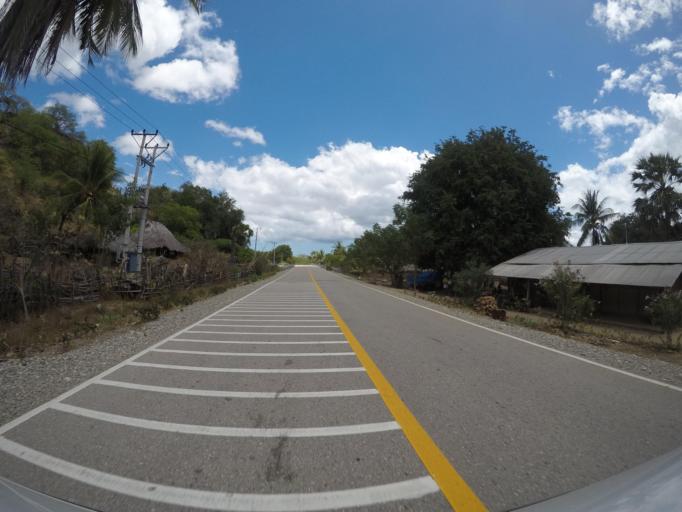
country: TL
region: Lautem
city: Lospalos
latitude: -8.4162
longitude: 126.7924
